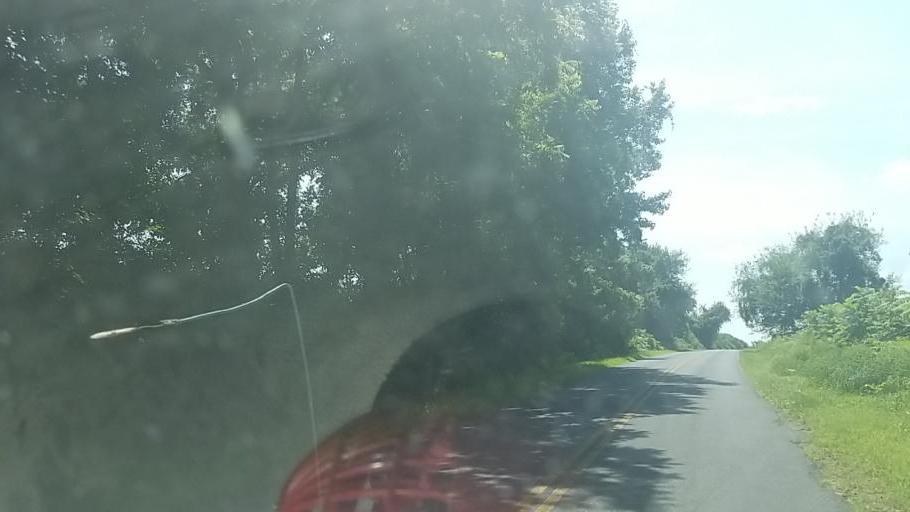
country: US
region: Maryland
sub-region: Caroline County
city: Ridgely
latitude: 38.9091
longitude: -75.9352
